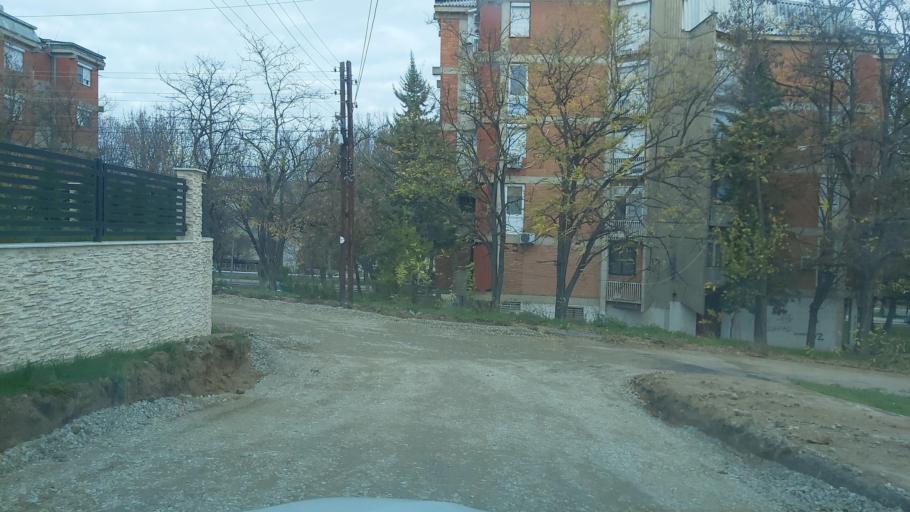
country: MK
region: Negotino
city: Negotino
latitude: 41.4820
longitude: 22.0812
